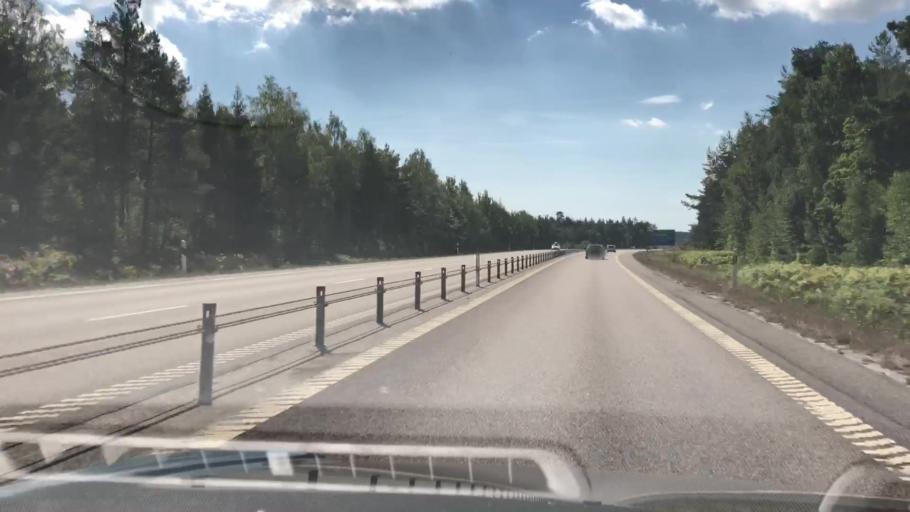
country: SE
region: Kalmar
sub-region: Kalmar Kommun
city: Lindsdal
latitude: 56.7252
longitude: 16.3155
